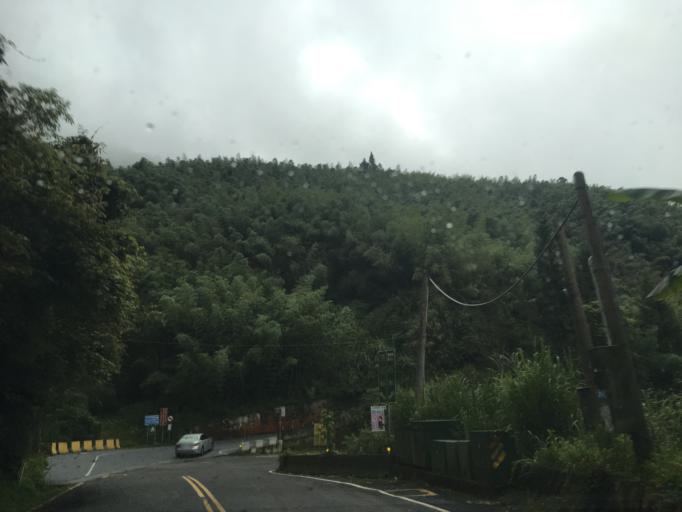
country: TW
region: Taiwan
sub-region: Chiayi
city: Jiayi Shi
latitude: 23.4865
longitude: 120.7000
